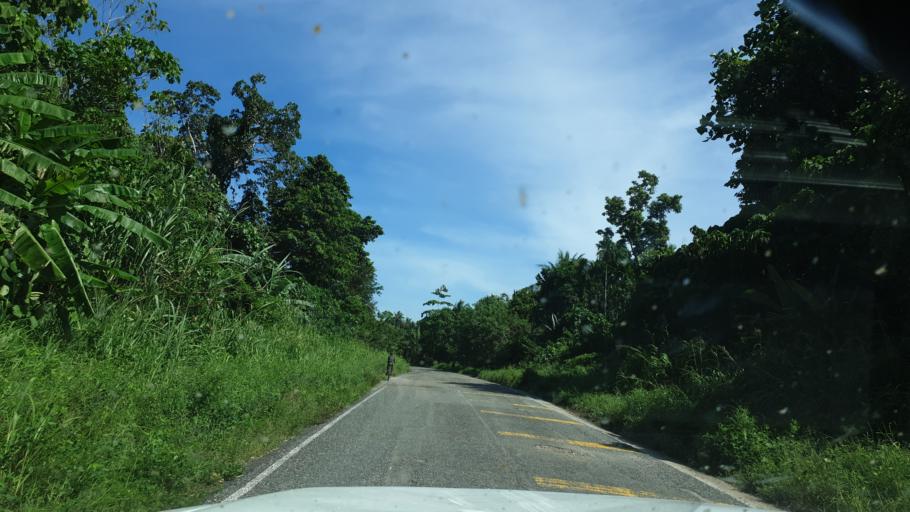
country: PG
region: Madang
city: Madang
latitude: -4.7090
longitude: 145.6246
